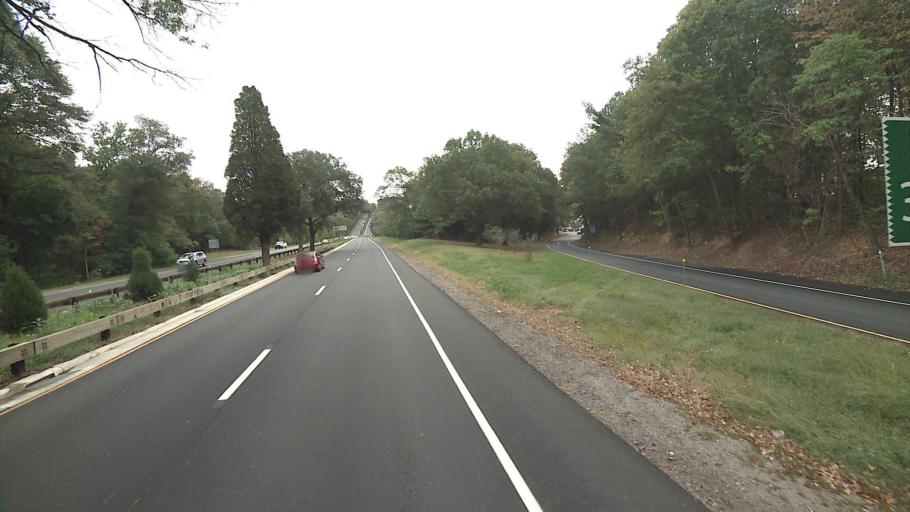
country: US
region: Connecticut
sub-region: Fairfield County
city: North Stamford
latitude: 41.1106
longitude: -73.5497
